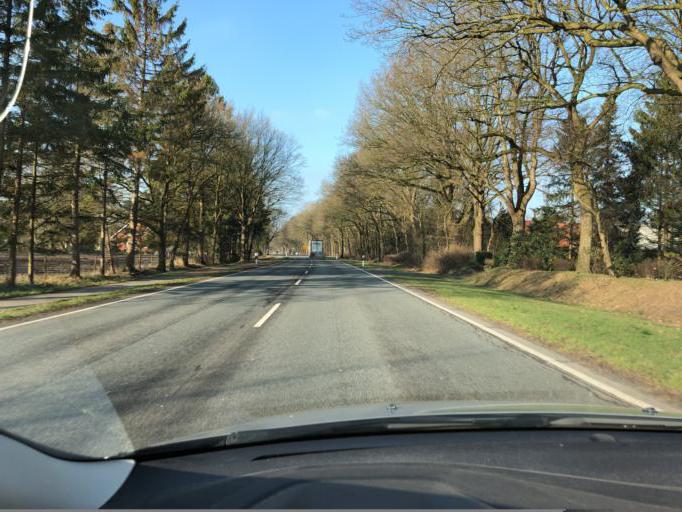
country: DE
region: Lower Saxony
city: Westerstede
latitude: 53.2927
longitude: 7.8712
